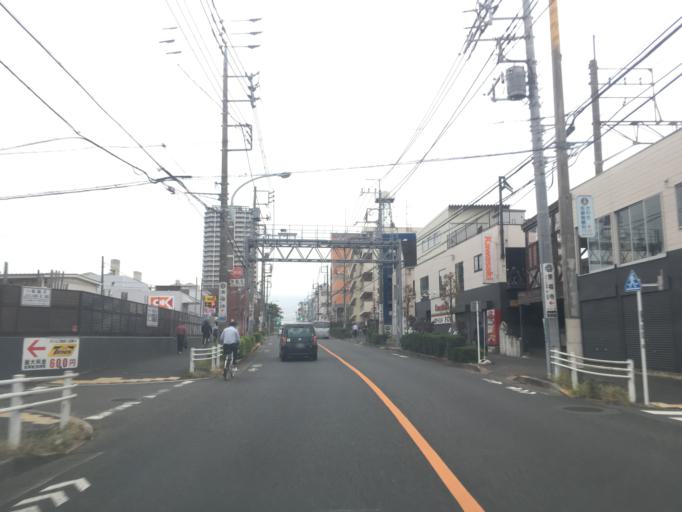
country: JP
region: Tokyo
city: Kokubunji
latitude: 35.7024
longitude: 139.4661
